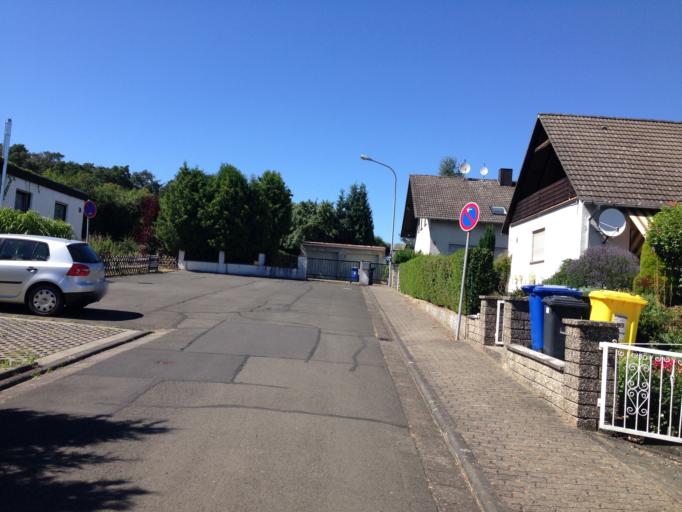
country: DE
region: Hesse
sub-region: Regierungsbezirk Giessen
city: Grossen Buseck
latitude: 50.5908
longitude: 8.7982
